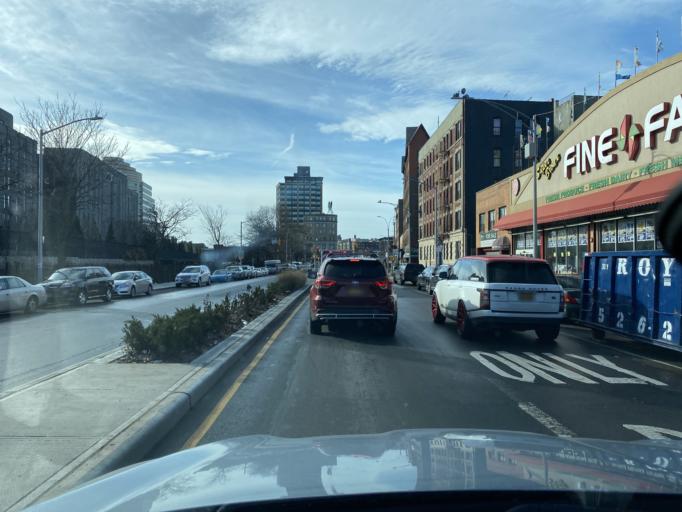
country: US
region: New York
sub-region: Bronx
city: The Bronx
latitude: 40.8637
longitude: -73.8888
